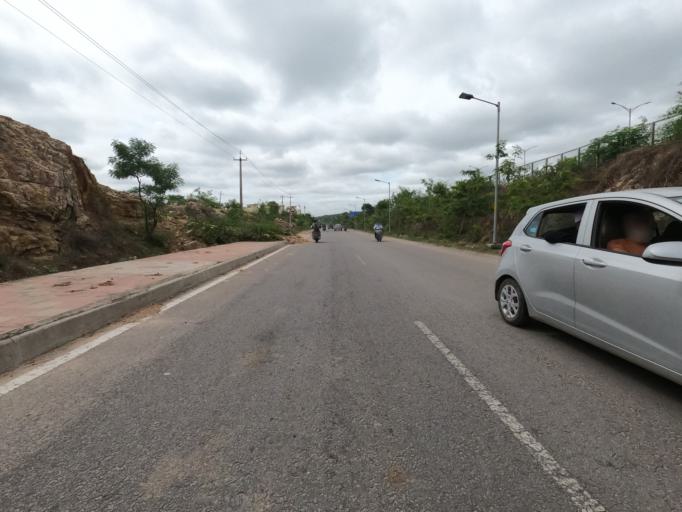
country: IN
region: Telangana
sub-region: Hyderabad
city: Hyderabad
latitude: 17.3333
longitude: 78.3702
